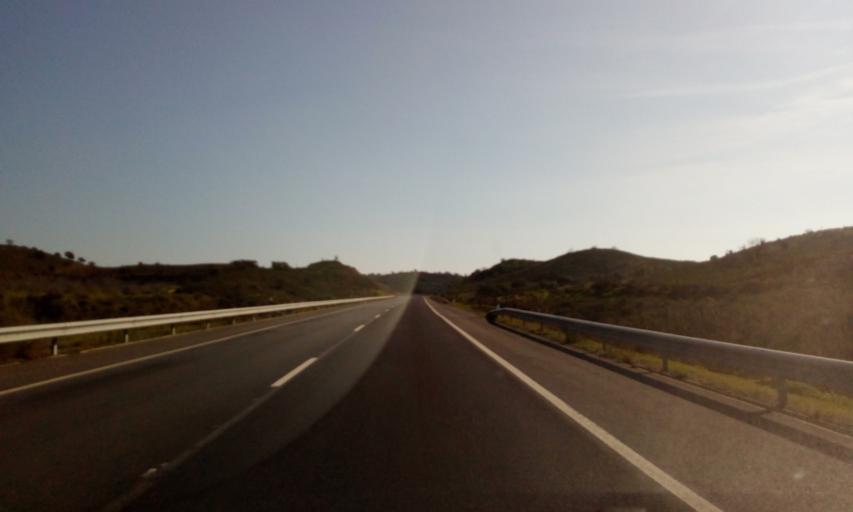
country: PT
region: Faro
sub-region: Castro Marim
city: Castro Marim
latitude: 37.2495
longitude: -7.4733
